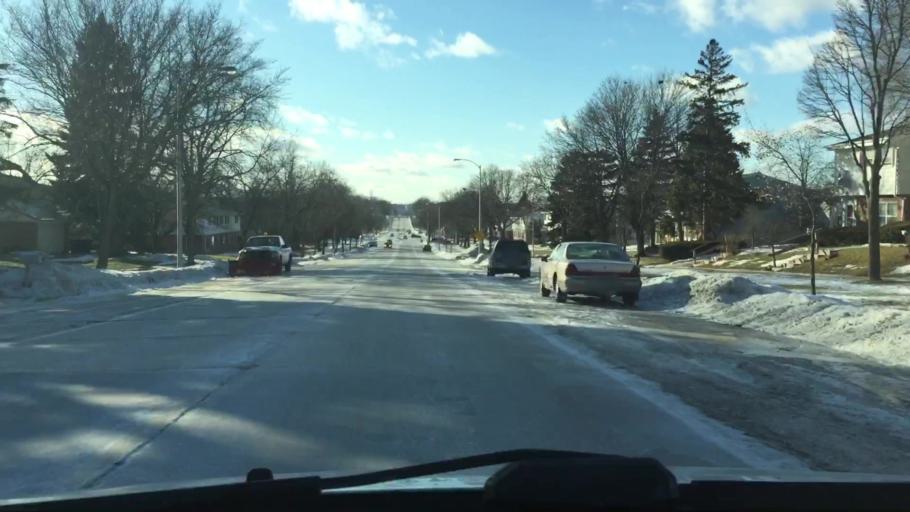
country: US
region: Wisconsin
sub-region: Milwaukee County
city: Greenfield
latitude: 42.9738
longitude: -88.0227
